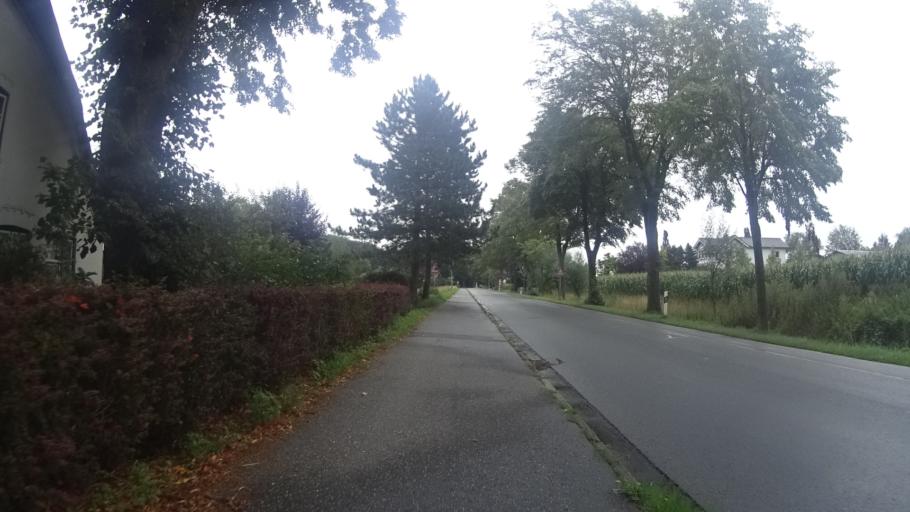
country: DE
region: Schleswig-Holstein
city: Seeth-Ekholt
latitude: 53.7556
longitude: 9.7250
